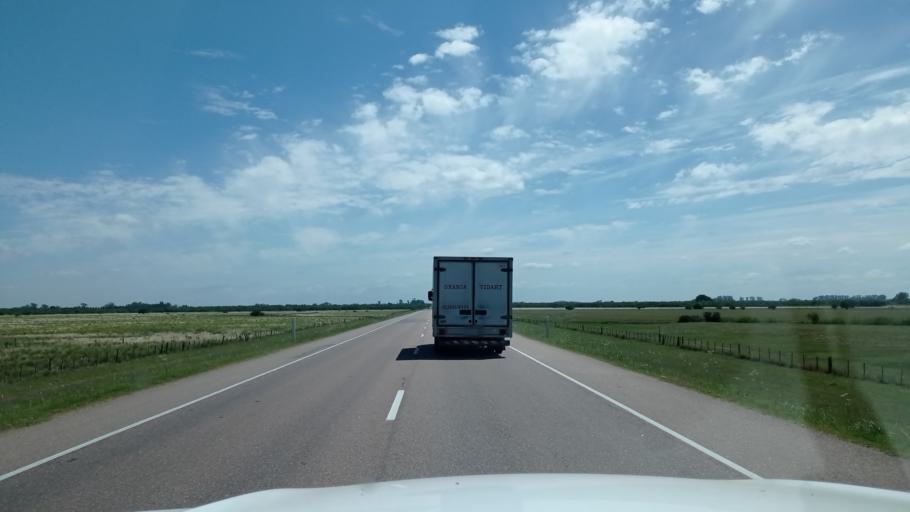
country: UY
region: Canelones
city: Canelones
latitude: -34.3799
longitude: -56.2530
